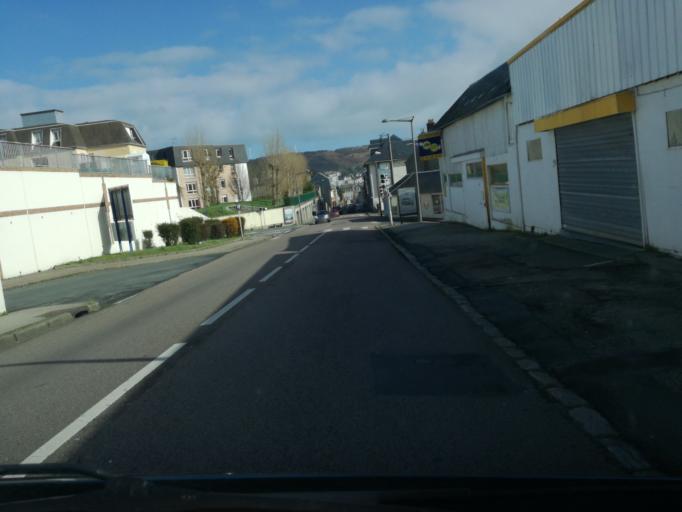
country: FR
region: Haute-Normandie
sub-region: Departement de la Seine-Maritime
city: Fecamp
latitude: 49.7538
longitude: 0.3726
